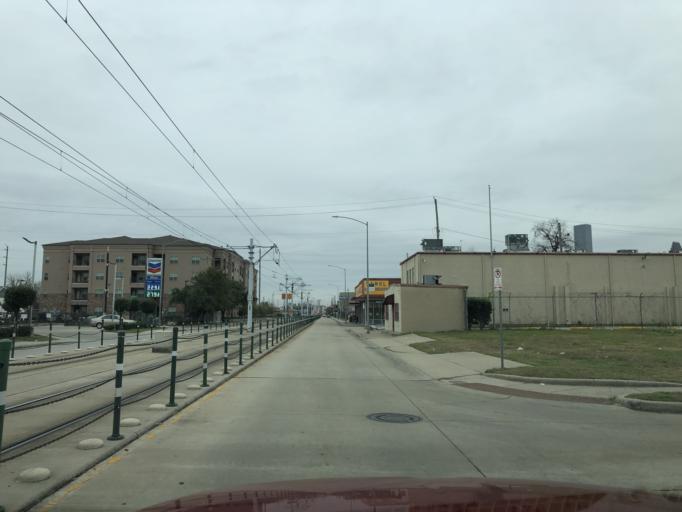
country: US
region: Texas
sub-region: Harris County
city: Houston
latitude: 29.7791
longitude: -95.3631
